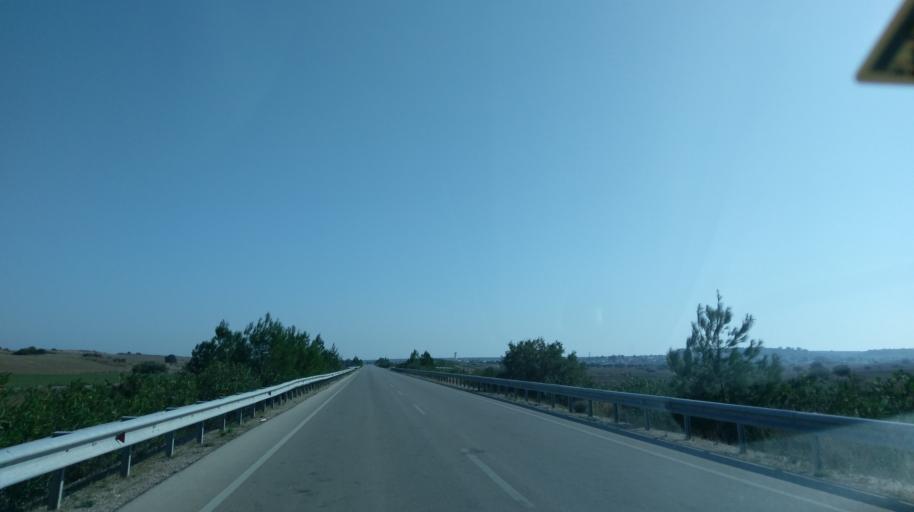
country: CY
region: Ammochostos
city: Leonarisso
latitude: 35.3816
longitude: 34.0196
